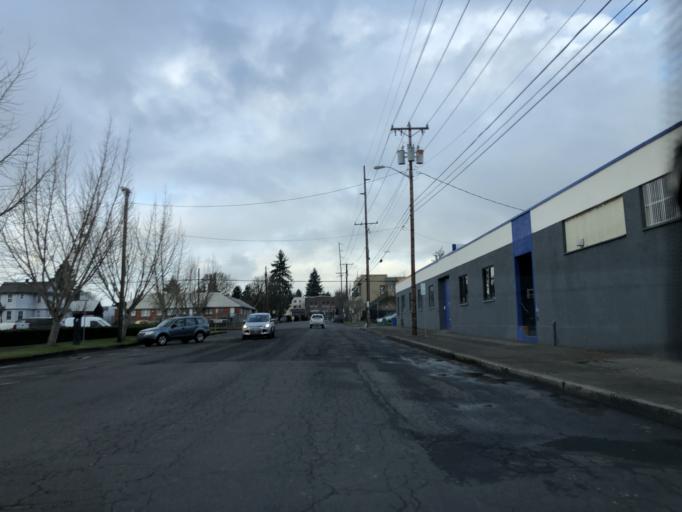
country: US
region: Washington
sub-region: Clark County
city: Vancouver
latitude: 45.6297
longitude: -122.6814
